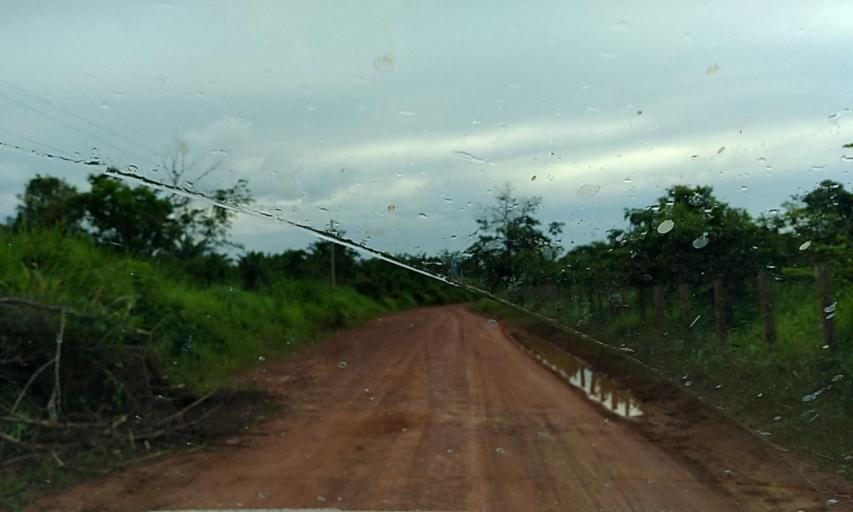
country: BR
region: Para
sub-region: Senador Jose Porfirio
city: Senador Jose Porfirio
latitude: -2.5519
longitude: -51.8658
